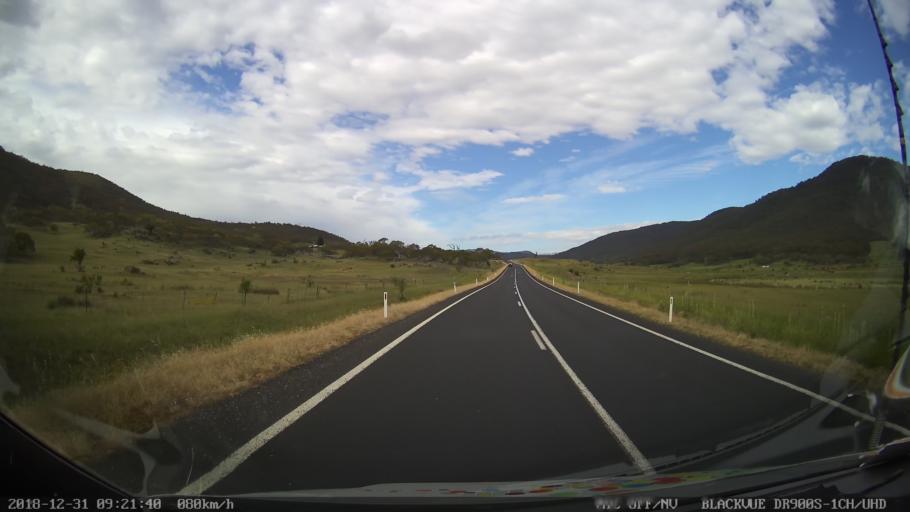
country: AU
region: New South Wales
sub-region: Snowy River
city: Jindabyne
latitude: -36.4305
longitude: 148.5581
